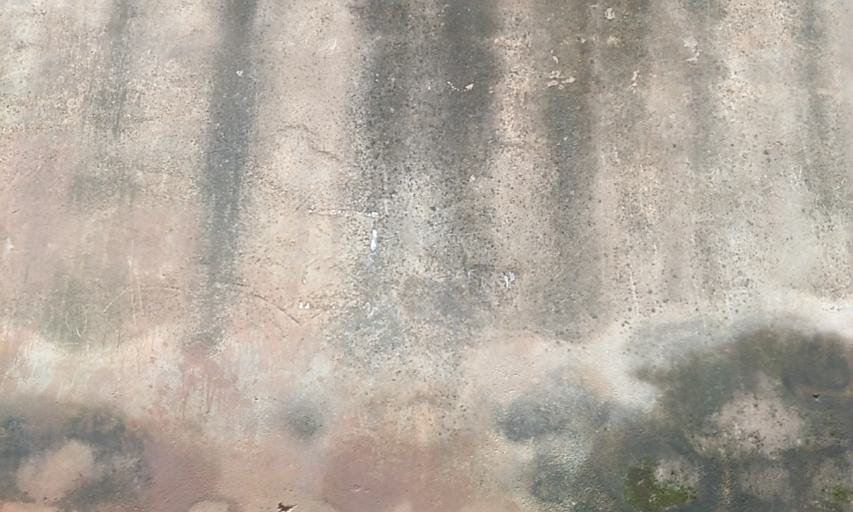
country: UG
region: Central Region
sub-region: Kampala District
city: Kampala
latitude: 0.3185
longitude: 32.5929
